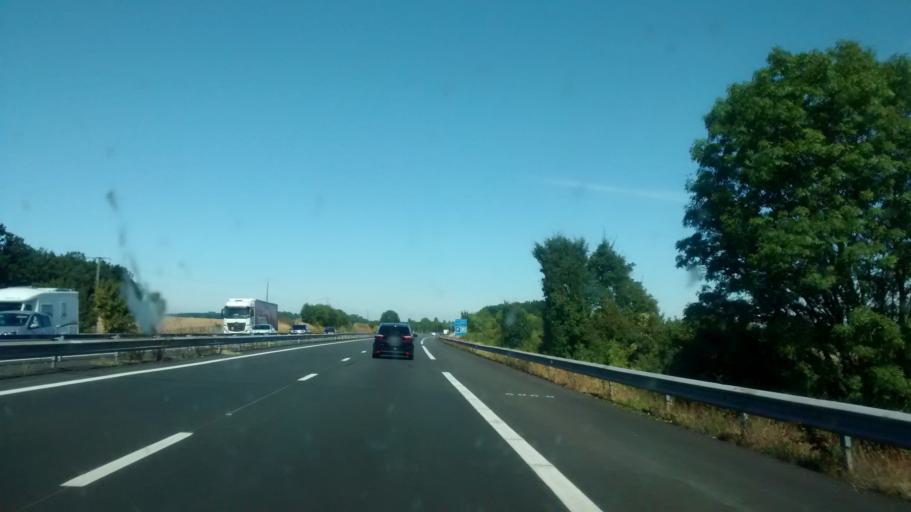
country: FR
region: Poitou-Charentes
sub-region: Departement des Deux-Sevres
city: Beauvoir-sur-Niort
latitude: 46.1050
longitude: -0.5353
